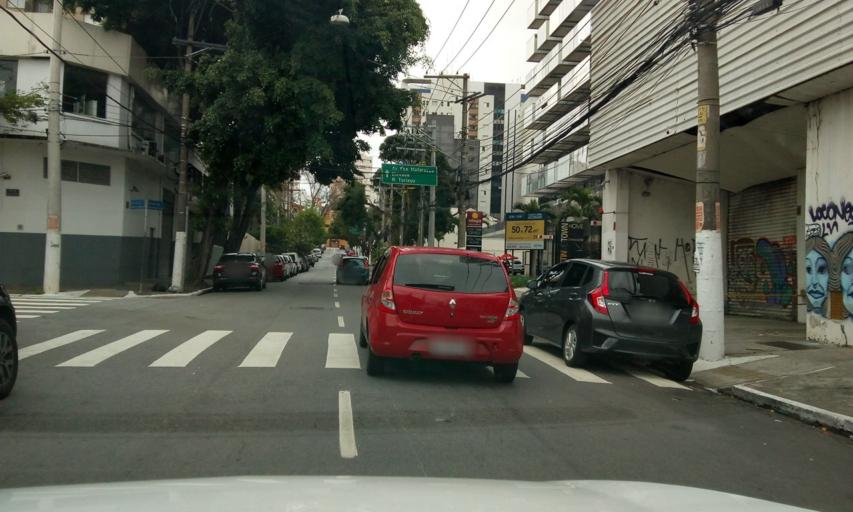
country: BR
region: Sao Paulo
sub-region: Sao Paulo
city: Sao Paulo
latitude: -23.5286
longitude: -46.6624
